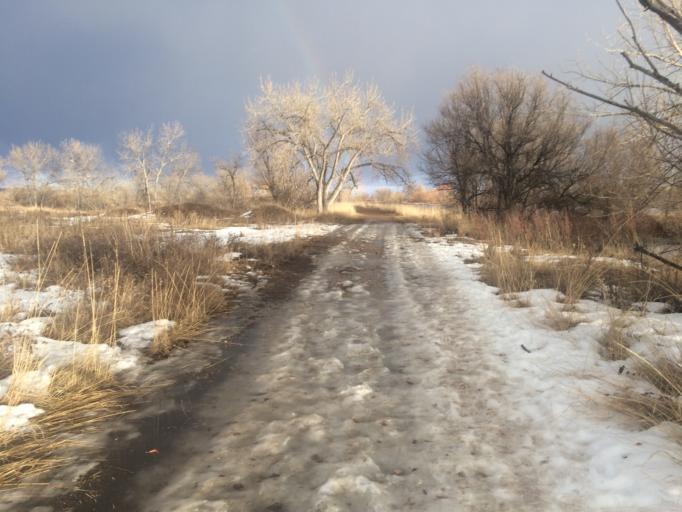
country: US
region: Colorado
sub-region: Boulder County
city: Gunbarrel
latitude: 40.0395
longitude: -105.1933
